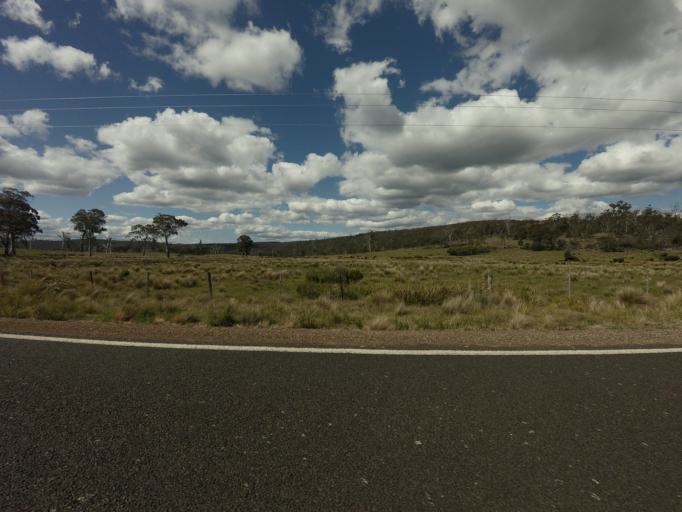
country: AU
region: Tasmania
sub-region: Northern Midlands
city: Evandale
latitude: -41.9490
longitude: 147.6065
